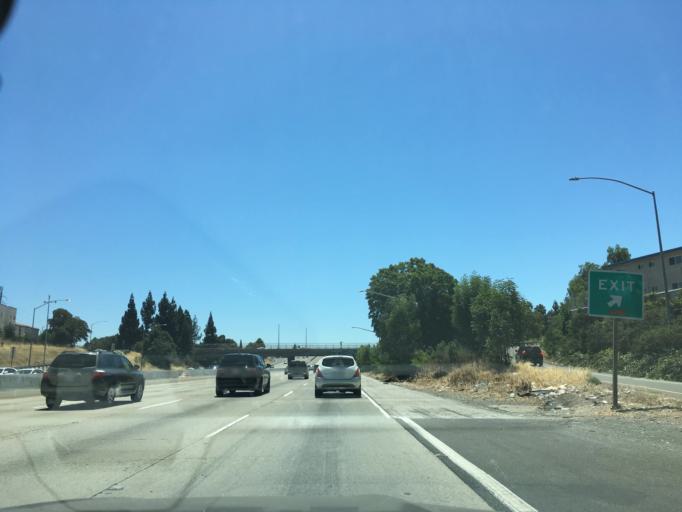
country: US
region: California
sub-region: Santa Clara County
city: Alum Rock
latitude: 37.3617
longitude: -121.8425
